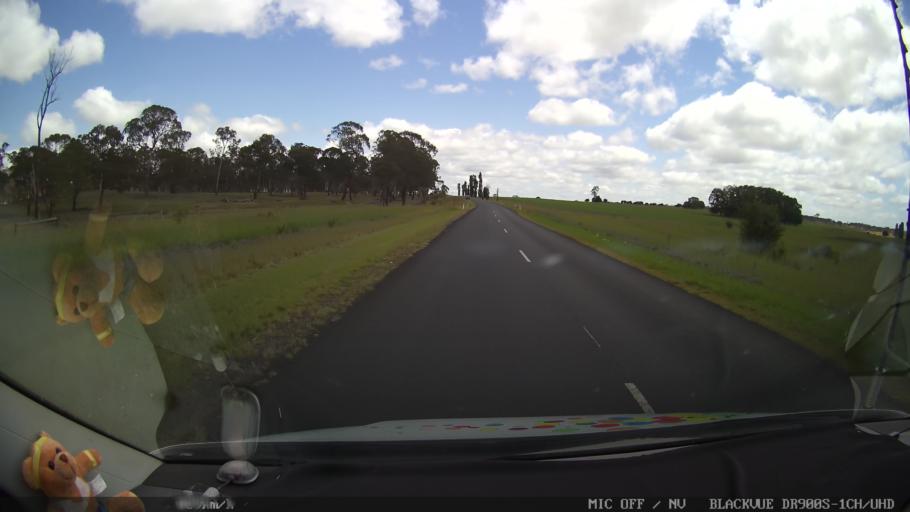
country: AU
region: New South Wales
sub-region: Glen Innes Severn
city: Glen Innes
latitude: -29.6666
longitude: 151.6940
